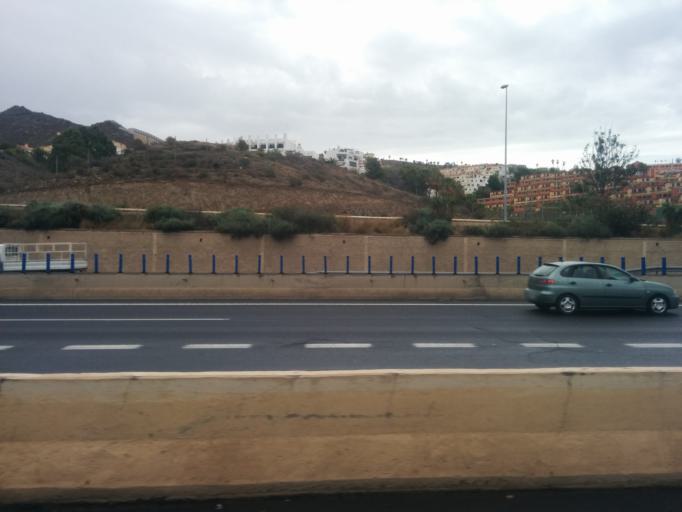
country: ES
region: Canary Islands
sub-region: Provincia de Santa Cruz de Tenerife
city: Playa de las Americas
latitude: 28.0852
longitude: -16.7291
